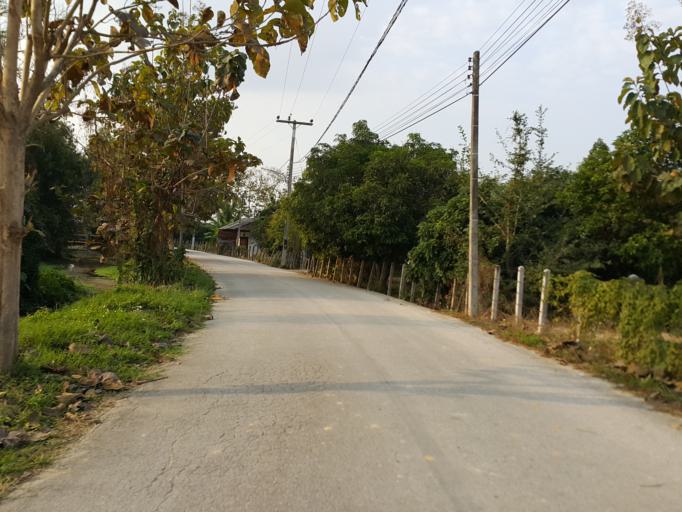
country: TH
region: Chiang Mai
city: San Sai
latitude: 18.8247
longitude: 99.0902
